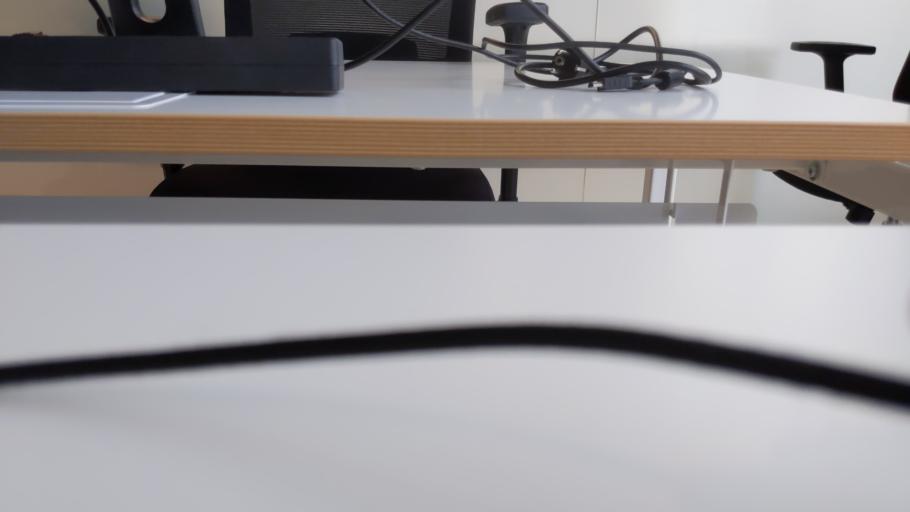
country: RU
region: Moskovskaya
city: Shevlyakovo
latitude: 56.4228
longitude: 36.9925
